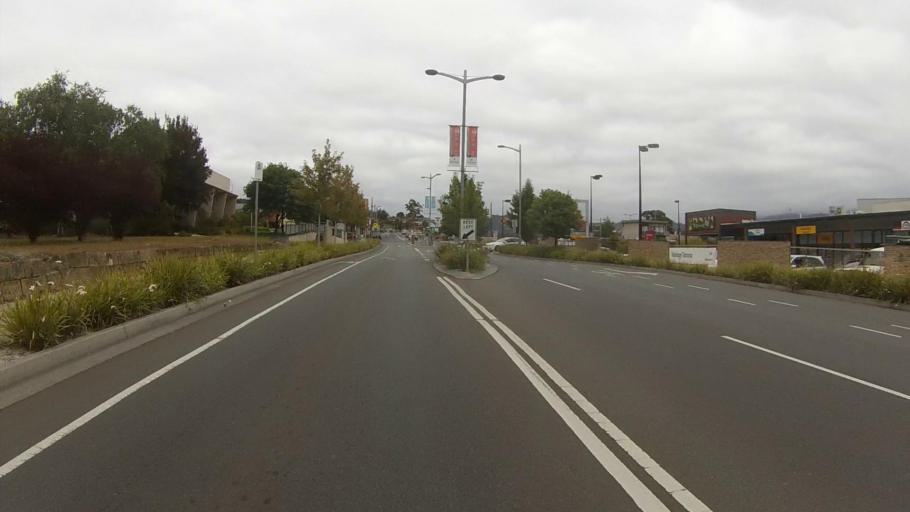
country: AU
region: Tasmania
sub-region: Kingborough
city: Kingston Beach
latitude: -42.9751
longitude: 147.3126
